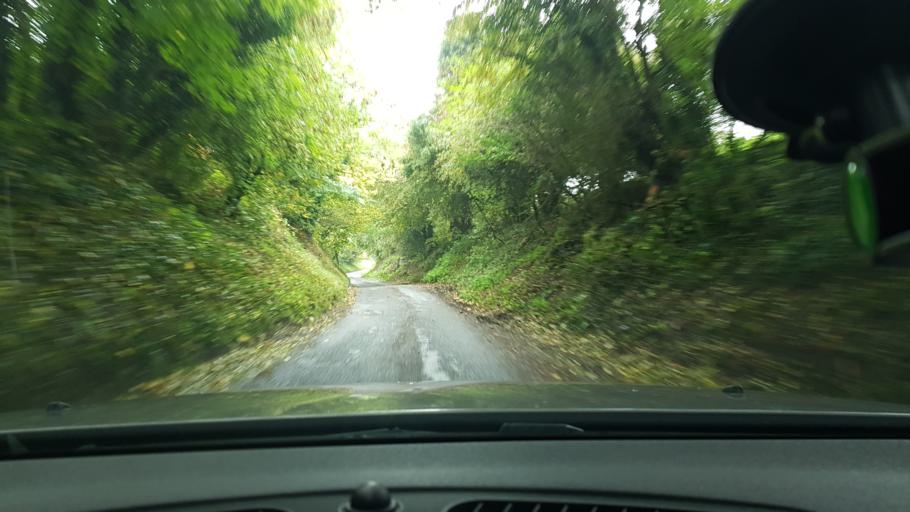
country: GB
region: England
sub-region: Wiltshire
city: Burbage
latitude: 51.3534
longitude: -1.7011
